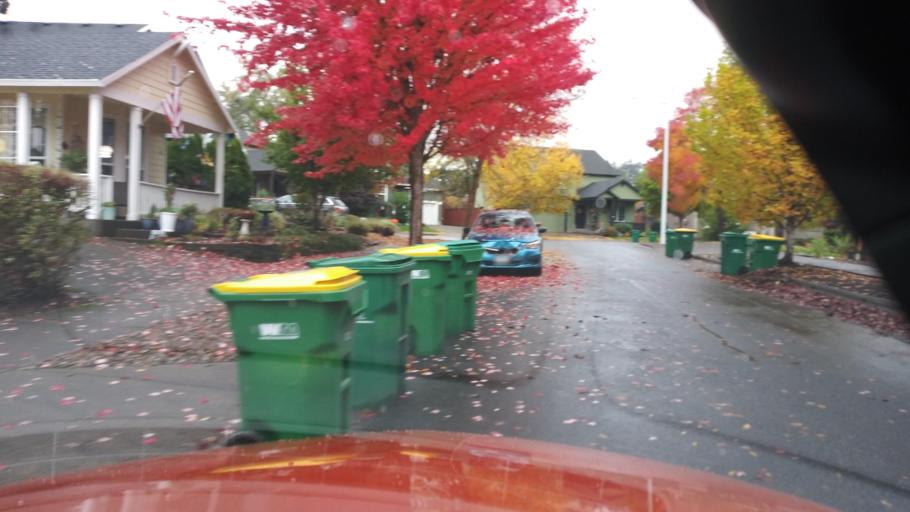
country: US
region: Oregon
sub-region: Washington County
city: Forest Grove
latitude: 45.5354
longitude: -123.1279
